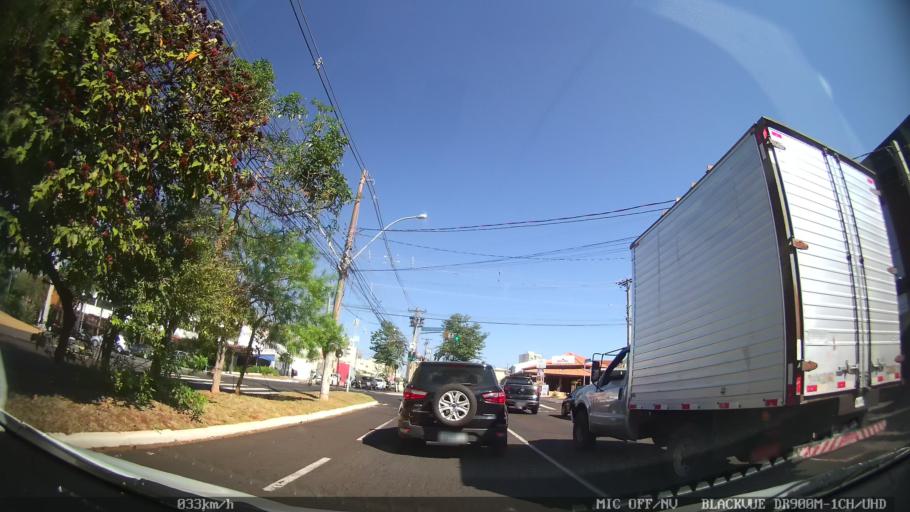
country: BR
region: Sao Paulo
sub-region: Ribeirao Preto
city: Ribeirao Preto
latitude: -21.2004
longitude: -47.8028
